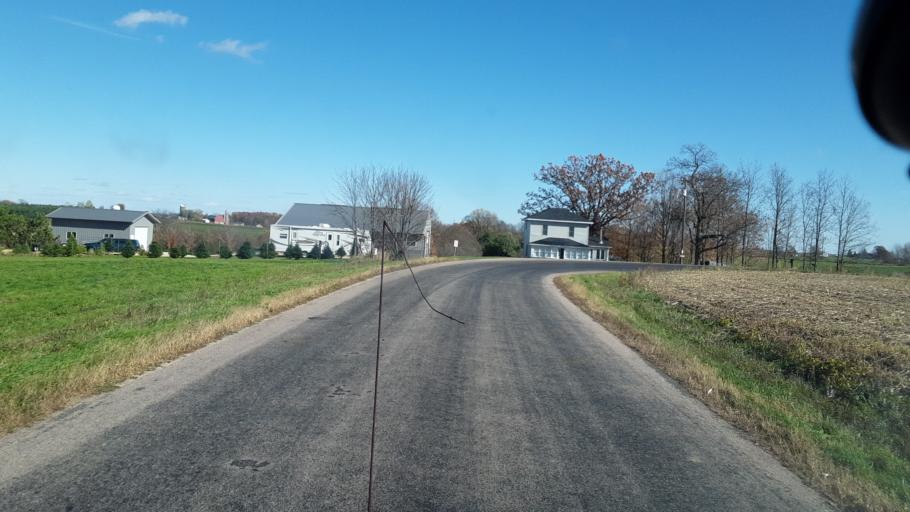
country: US
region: Wisconsin
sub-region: Vernon County
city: Hillsboro
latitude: 43.6969
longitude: -90.4436
